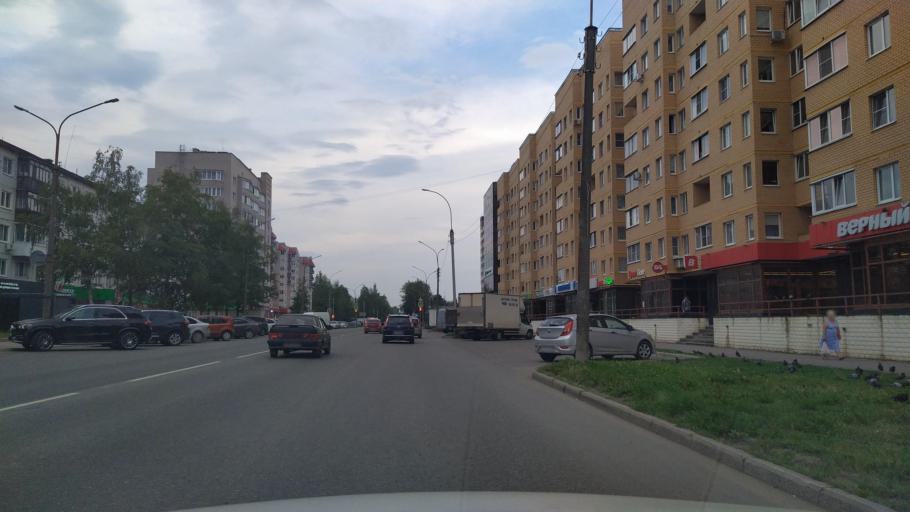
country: RU
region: Novgorod
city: Velikiy Novgorod
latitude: 58.5152
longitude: 31.2446
